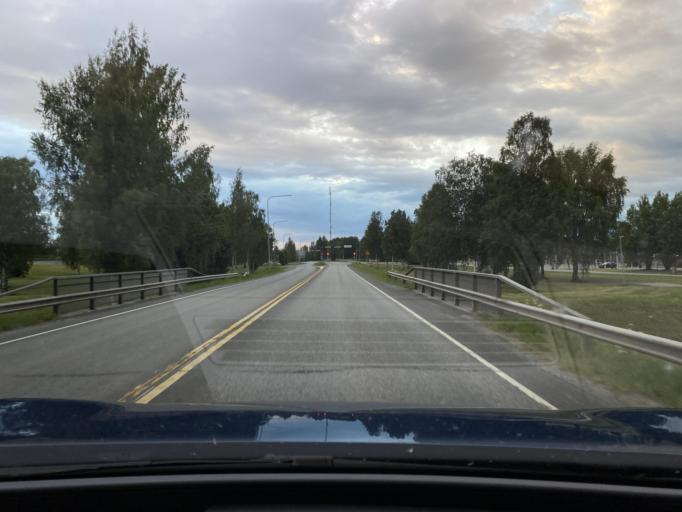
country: FI
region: Northern Ostrobothnia
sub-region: Raahe
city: Raahe
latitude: 64.6758
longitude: 24.4833
